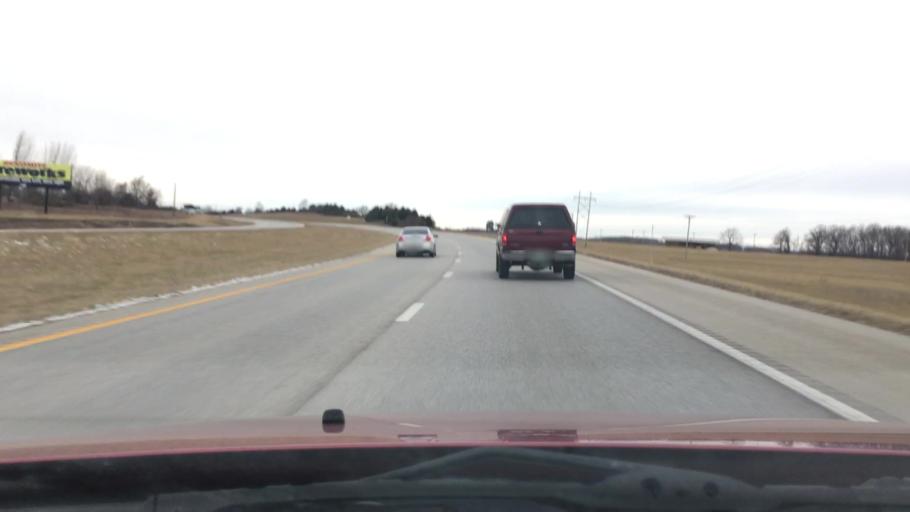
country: US
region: Missouri
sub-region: Webster County
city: Seymour
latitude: 37.1557
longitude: -92.7606
